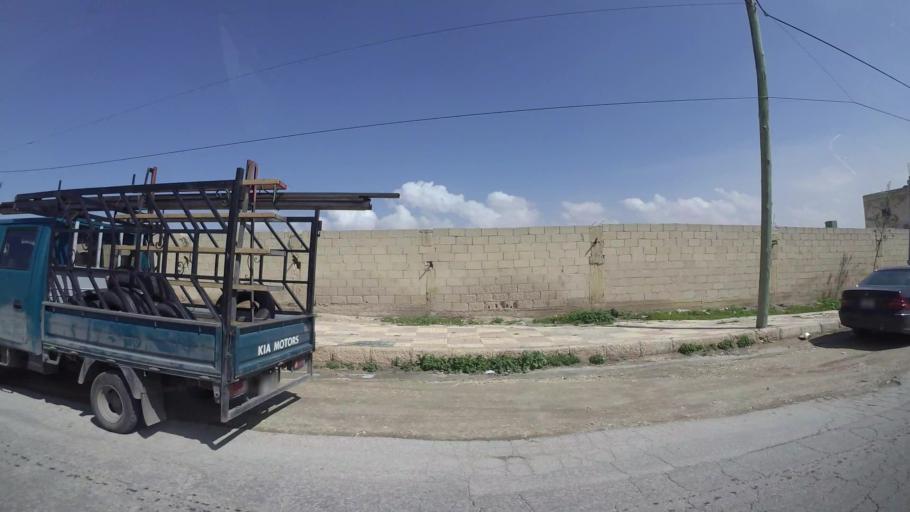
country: JO
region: Zarqa
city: Russeifa
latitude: 31.9936
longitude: 36.0068
